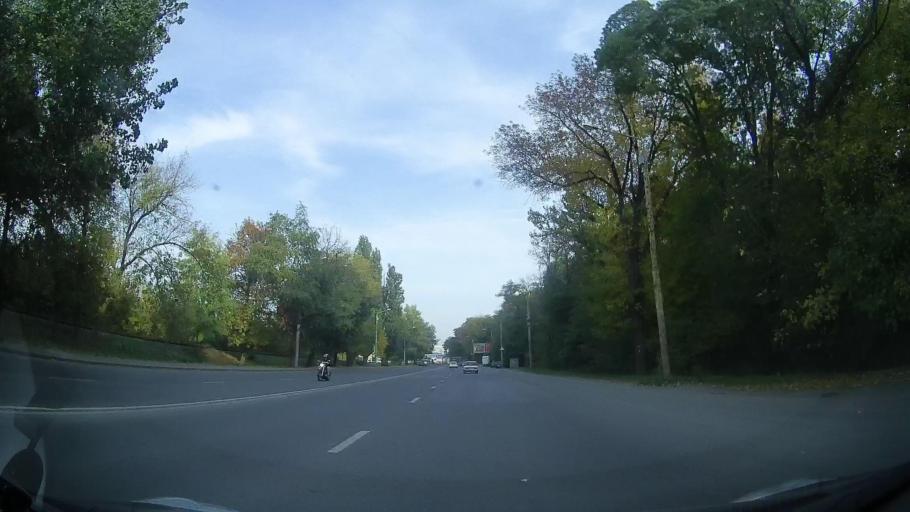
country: RU
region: Rostov
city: Aksay
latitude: 47.2750
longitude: 39.8128
